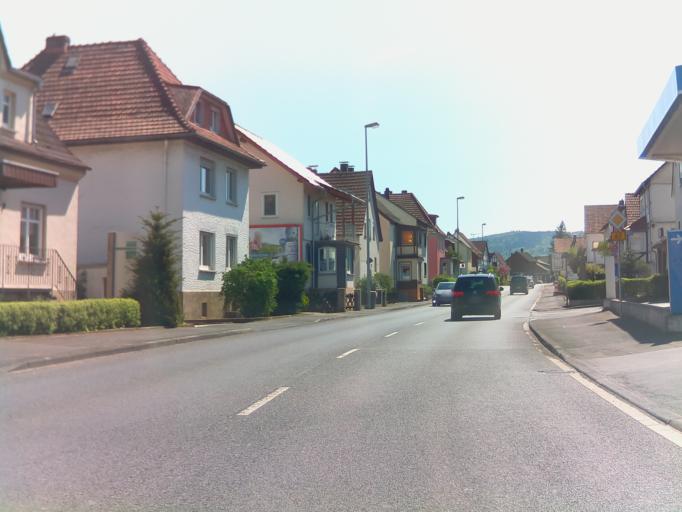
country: DE
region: Hesse
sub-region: Regierungsbezirk Kassel
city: Bad Hersfeld
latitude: 50.8365
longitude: 9.6689
